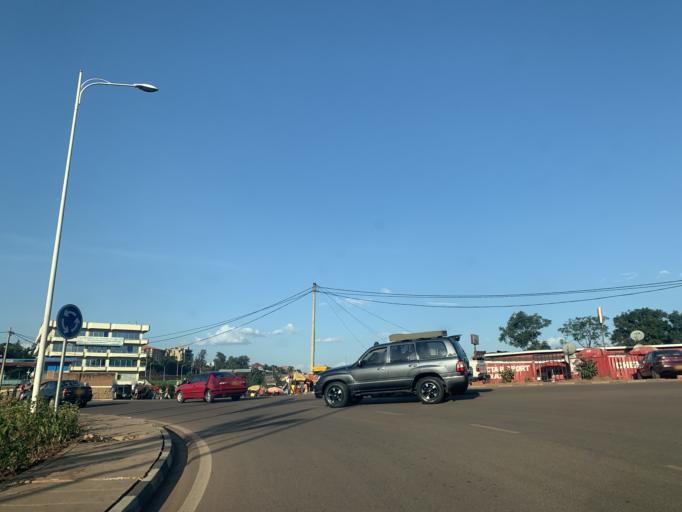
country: RW
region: Kigali
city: Kigali
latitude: -1.9676
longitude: 30.1026
